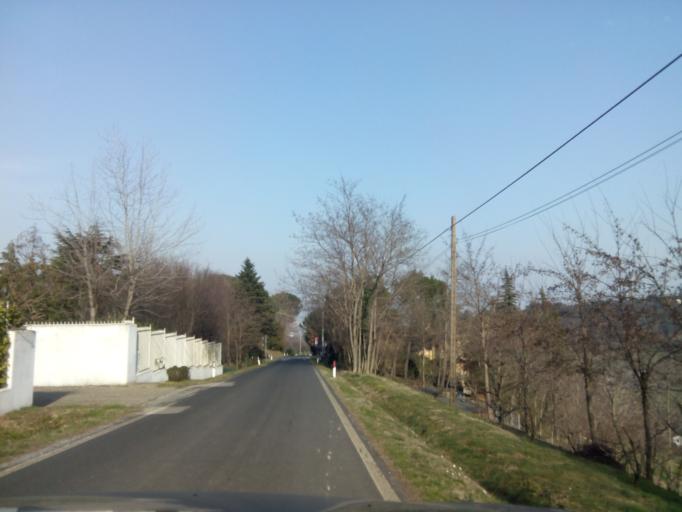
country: IT
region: Emilia-Romagna
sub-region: Provincia di Bologna
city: Imola
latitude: 44.3294
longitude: 11.7000
